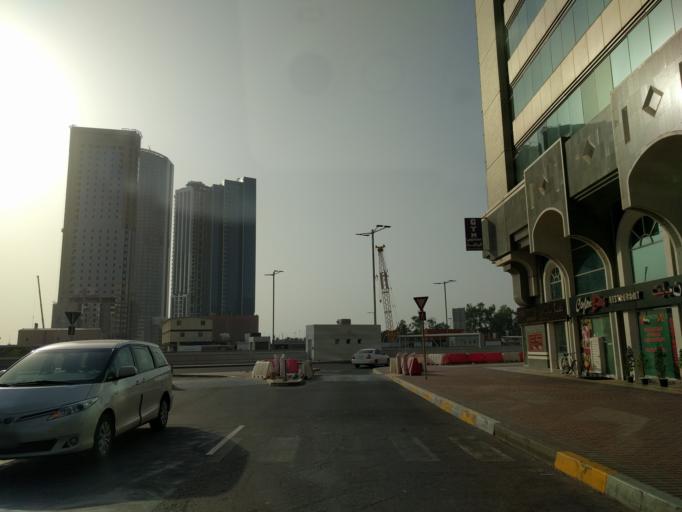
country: AE
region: Abu Dhabi
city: Abu Dhabi
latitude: 24.5018
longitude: 54.3732
